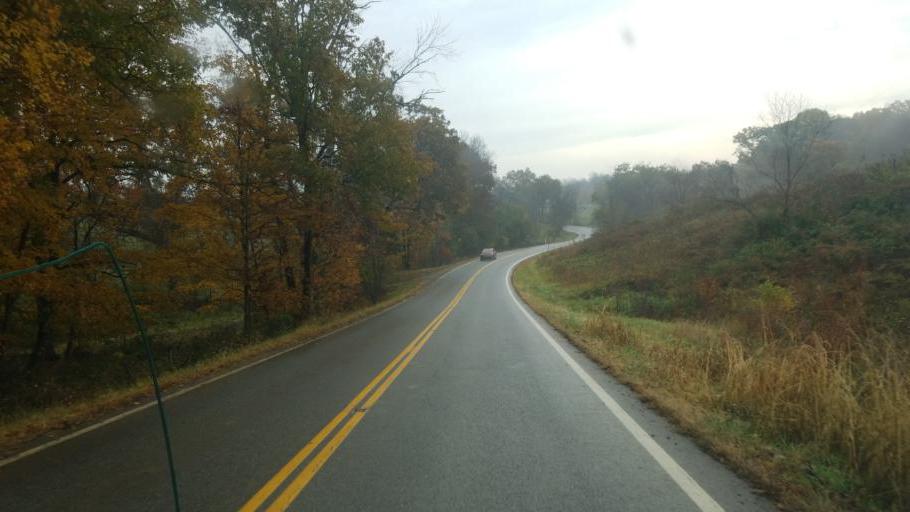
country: US
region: Ohio
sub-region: Morgan County
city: McConnelsville
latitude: 39.4736
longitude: -81.8814
